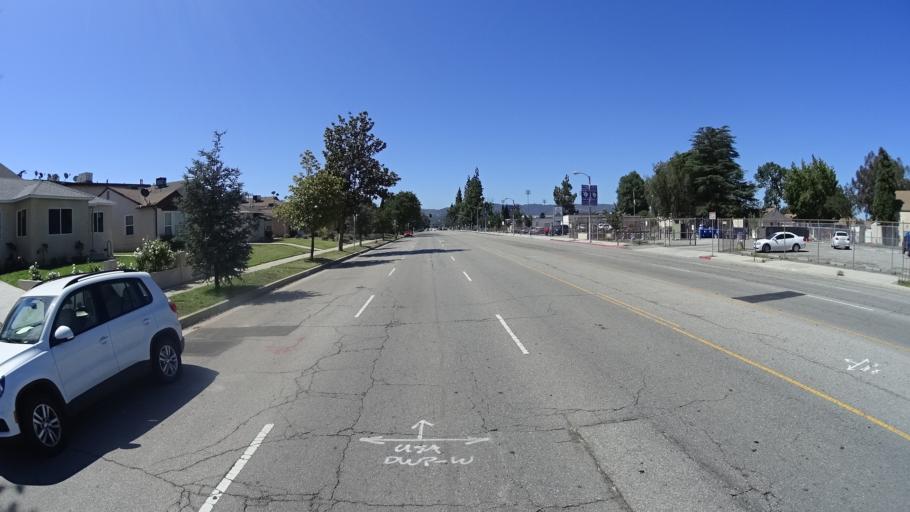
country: US
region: California
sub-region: Los Angeles County
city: Northridge
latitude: 34.1908
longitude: -118.5011
